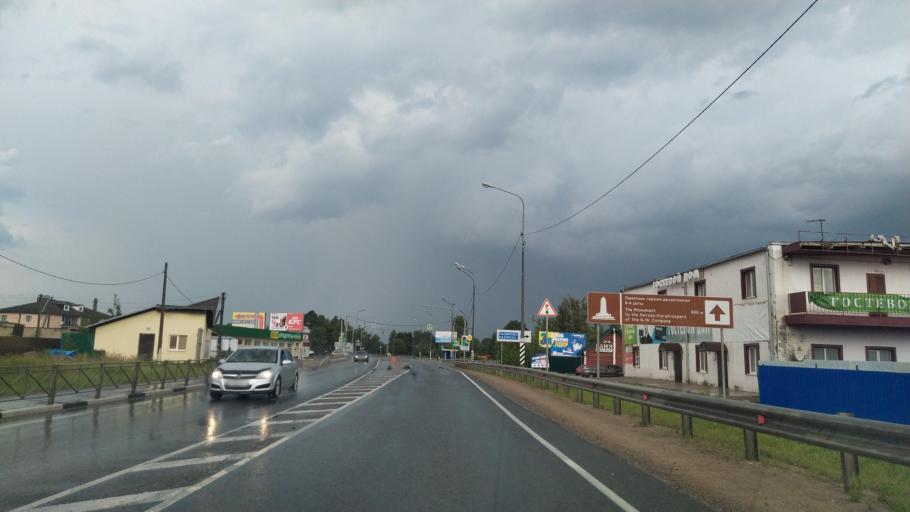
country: RU
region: Pskov
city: Pskov
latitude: 57.7436
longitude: 28.3699
